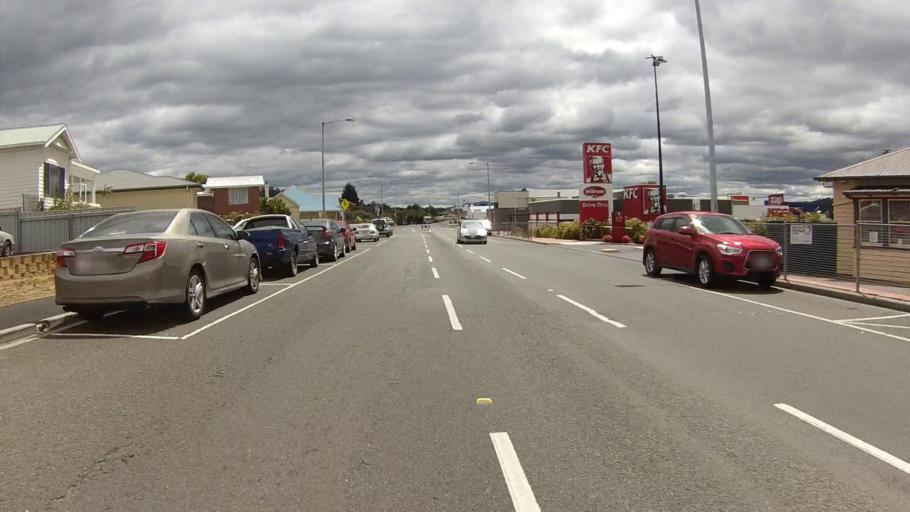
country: AU
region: Tasmania
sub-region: Glenorchy
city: Claremont
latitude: -42.7910
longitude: 147.2537
